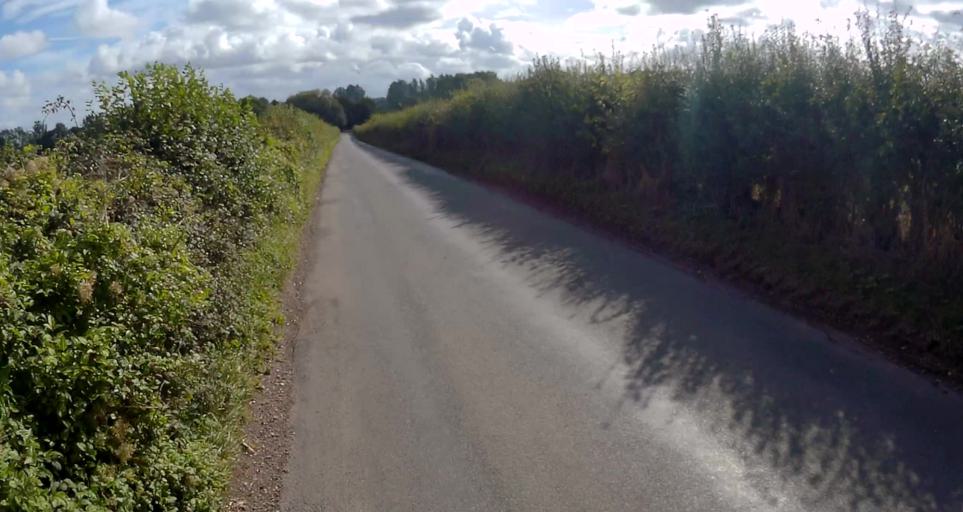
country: GB
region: England
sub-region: Hampshire
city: Kings Worthy
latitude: 51.0922
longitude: -1.2717
